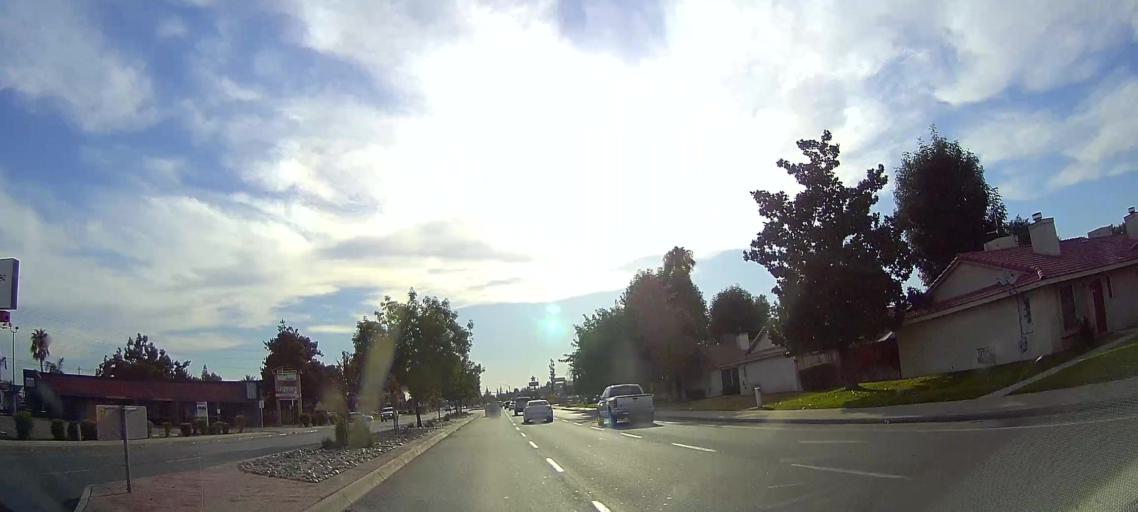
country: US
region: California
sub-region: Kern County
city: Bakersfield
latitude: 35.3179
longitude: -119.0537
